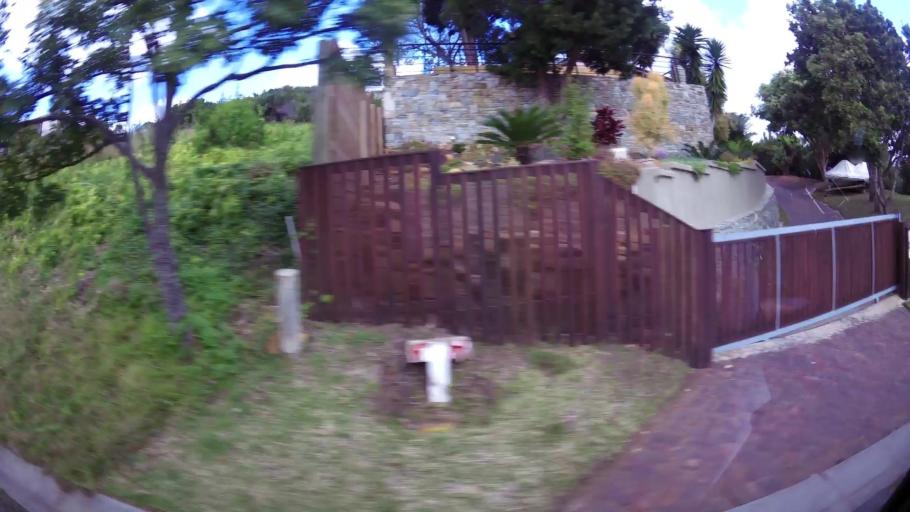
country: ZA
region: Western Cape
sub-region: Eden District Municipality
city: Knysna
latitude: -34.0653
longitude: 23.0796
